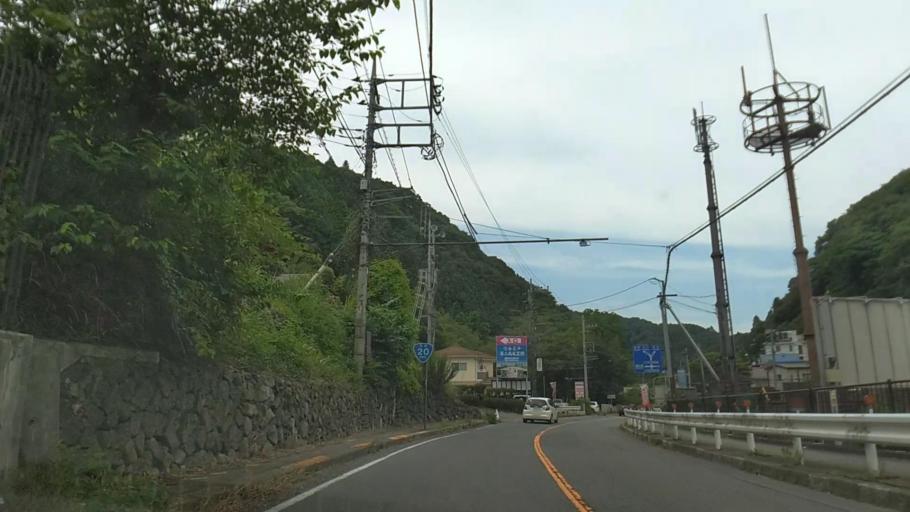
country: JP
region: Tokyo
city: Hachioji
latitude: 35.6200
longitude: 139.2624
